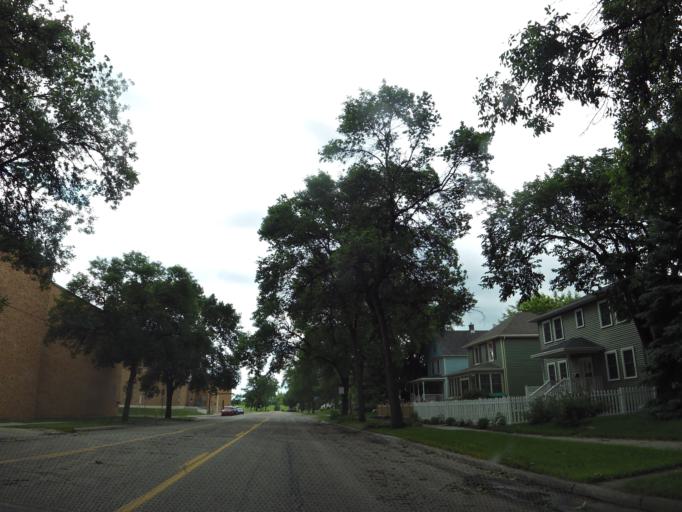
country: US
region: North Dakota
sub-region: Grand Forks County
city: Grand Forks
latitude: 47.9212
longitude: -97.0259
